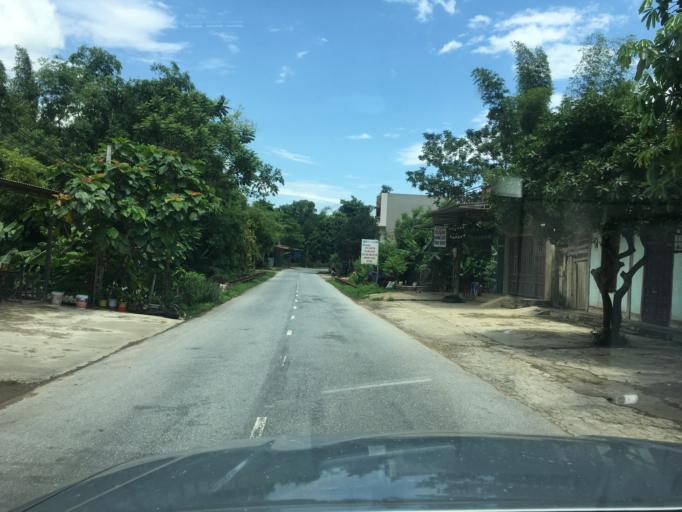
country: VN
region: Yen Bai
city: Son Thinh
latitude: 21.6553
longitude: 104.5000
